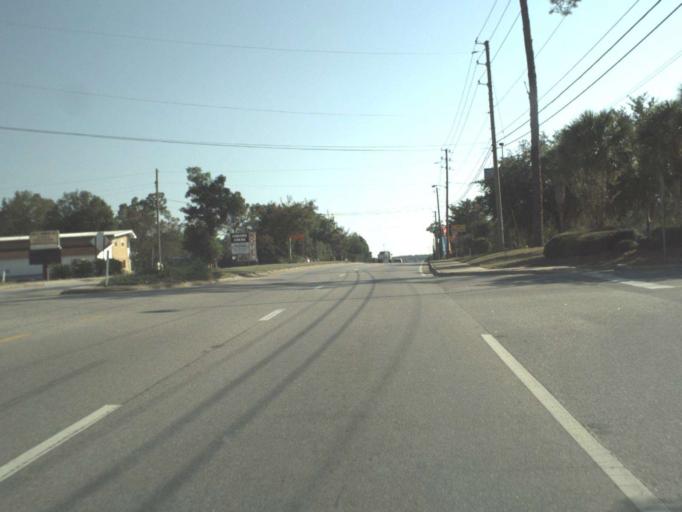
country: US
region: Florida
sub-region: Walton County
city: DeFuniak Springs
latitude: 30.7045
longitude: -86.1226
